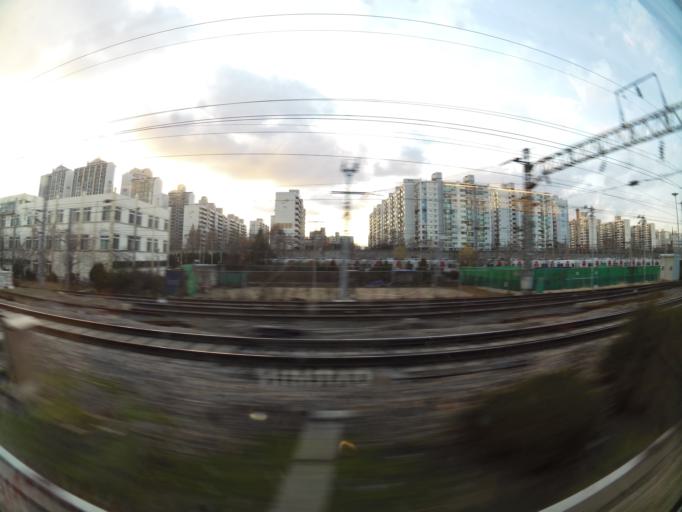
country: KR
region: Gyeonggi-do
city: Kwangmyong
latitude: 37.4919
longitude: 126.8796
